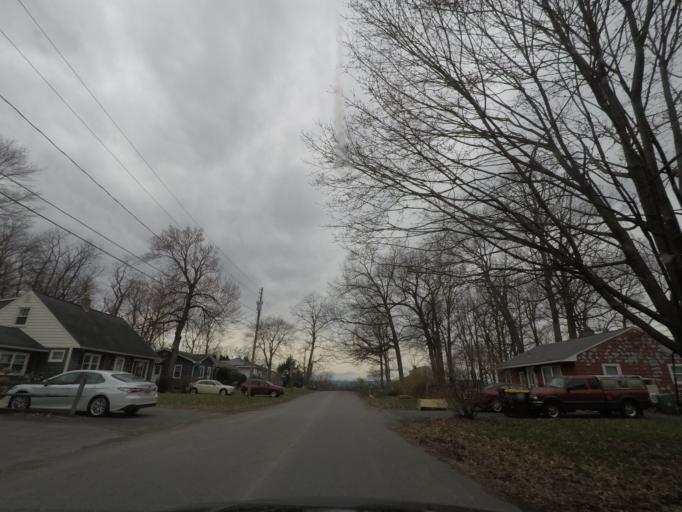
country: US
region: New York
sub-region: Rensselaer County
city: Hampton Manor
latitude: 42.6171
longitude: -73.7178
